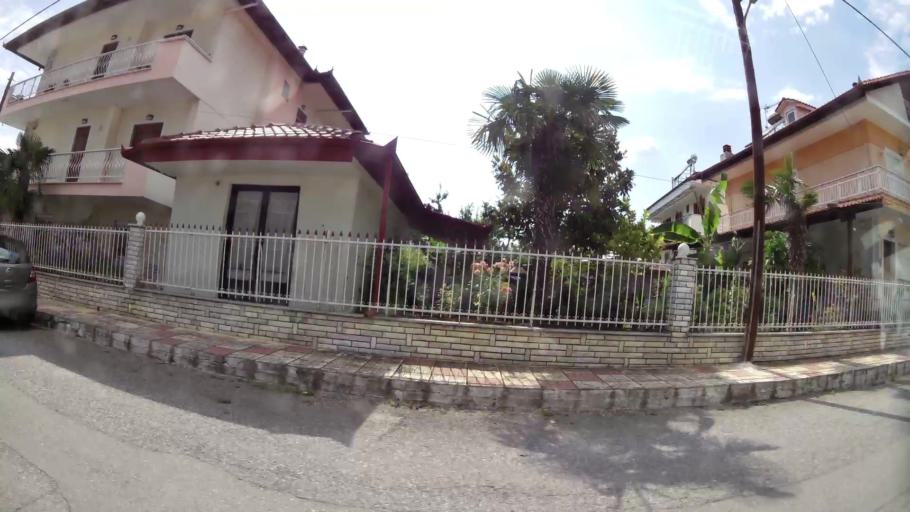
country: GR
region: Central Macedonia
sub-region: Nomos Pierias
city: Makrygialos
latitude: 40.4139
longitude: 22.6042
